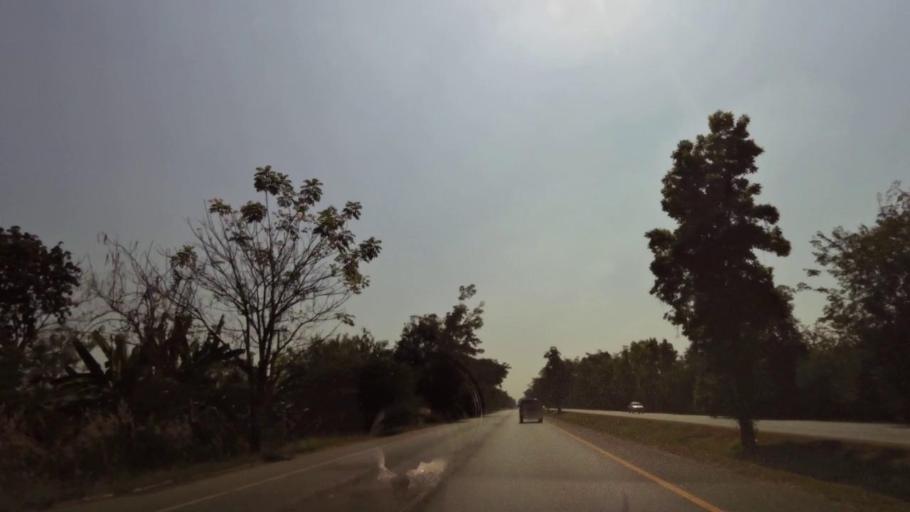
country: TH
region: Phichit
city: Bueng Na Rang
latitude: 16.3314
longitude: 100.1284
